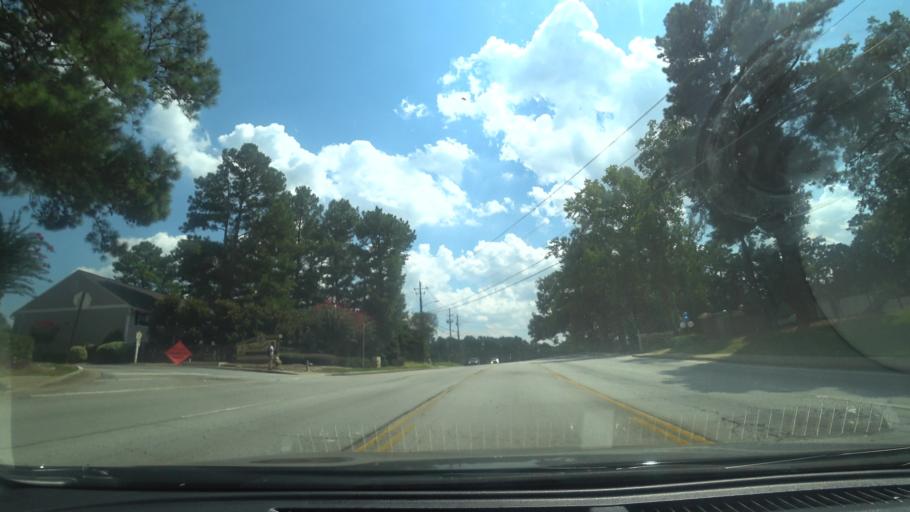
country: US
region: Georgia
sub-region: DeKalb County
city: Clarkston
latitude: 33.8209
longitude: -84.2316
